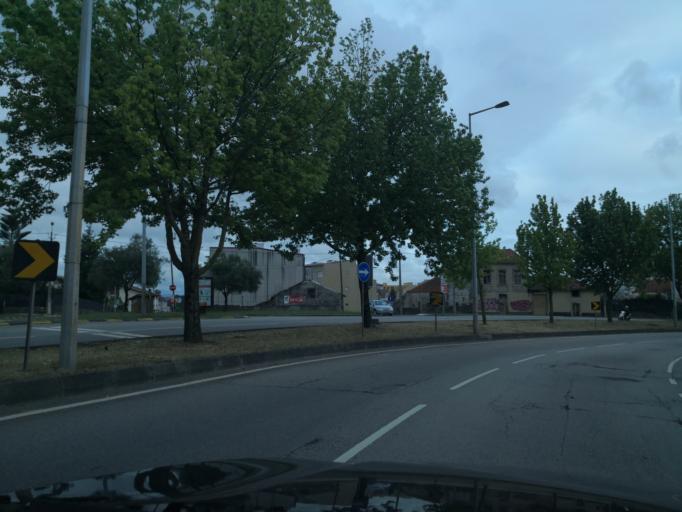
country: PT
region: Porto
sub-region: Gondomar
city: Rio Tinto
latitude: 41.1718
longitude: -8.5672
